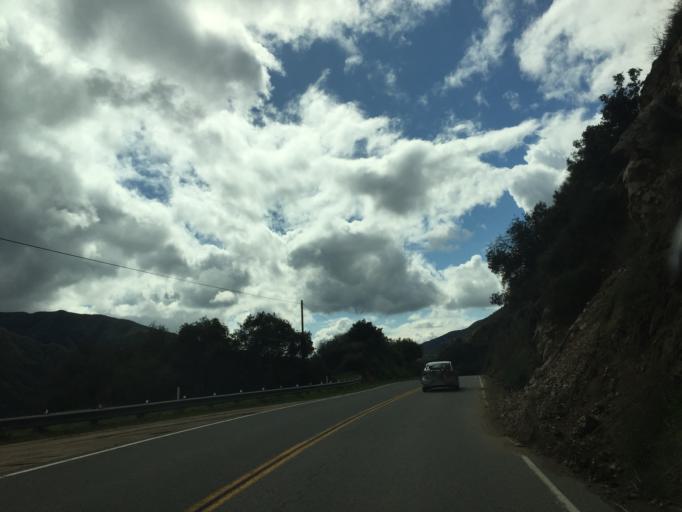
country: US
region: California
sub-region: Los Angeles County
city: Glendora
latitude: 34.2295
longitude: -117.8458
